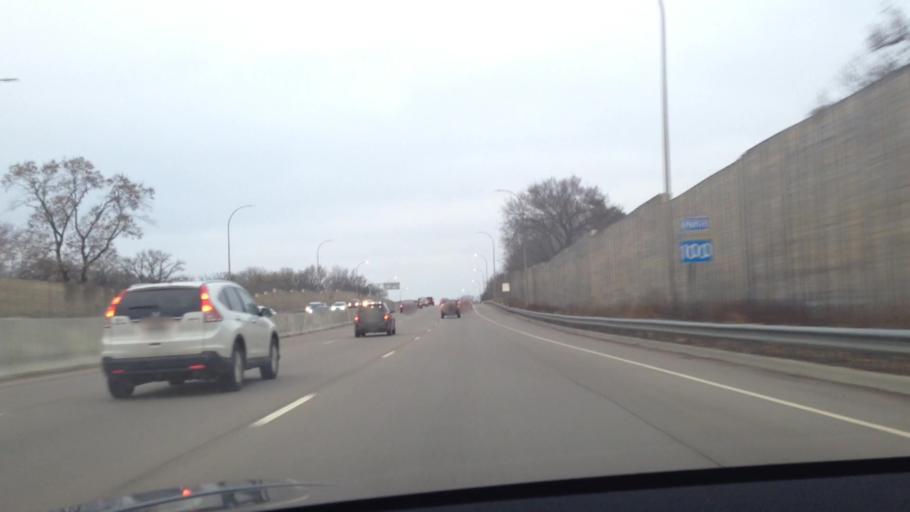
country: US
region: Minnesota
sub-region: Hennepin County
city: Edina
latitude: 44.9163
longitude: -93.3500
